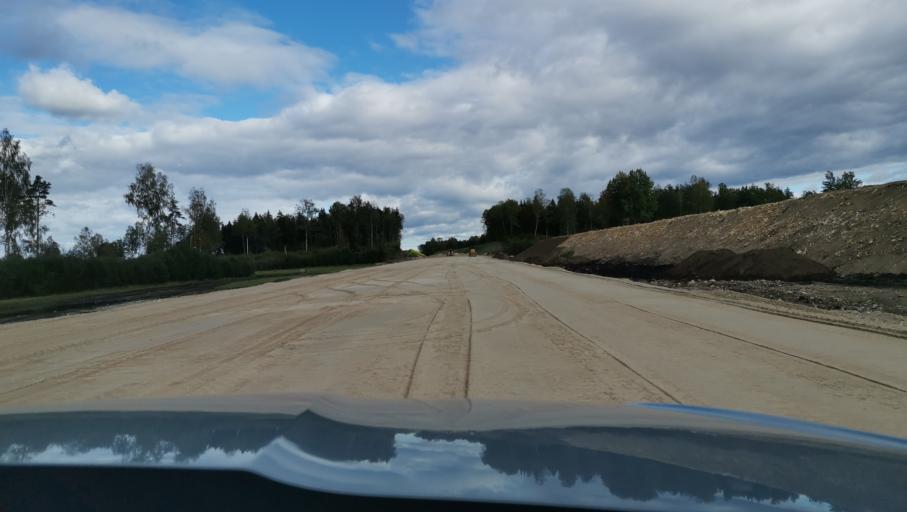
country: EE
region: Harju
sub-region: Keila linn
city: Keila
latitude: 59.1458
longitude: 24.4977
